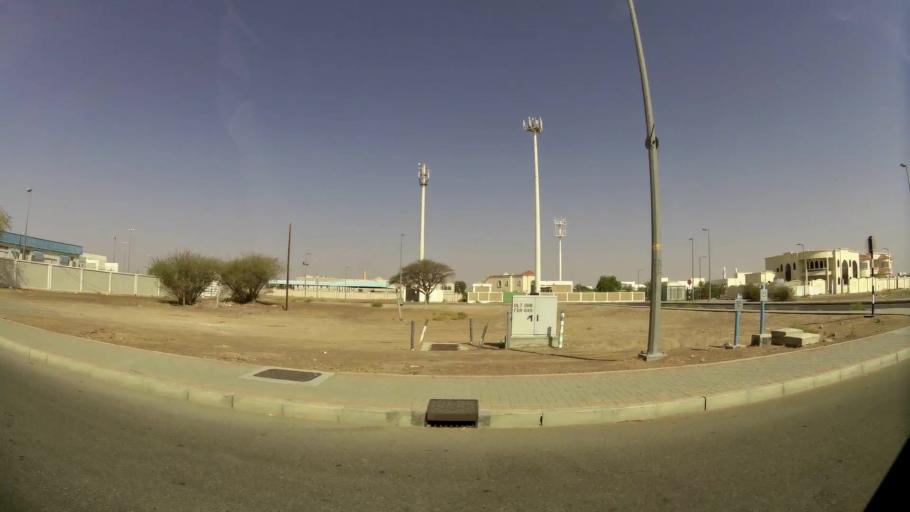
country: OM
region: Al Buraimi
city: Al Buraymi
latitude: 24.3419
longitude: 55.8026
